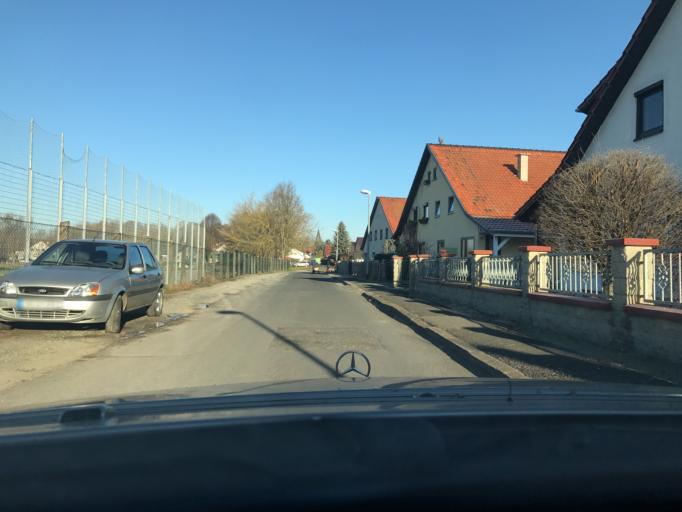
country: DE
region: Thuringia
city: Muehlhausen
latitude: 51.2306
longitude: 10.4489
